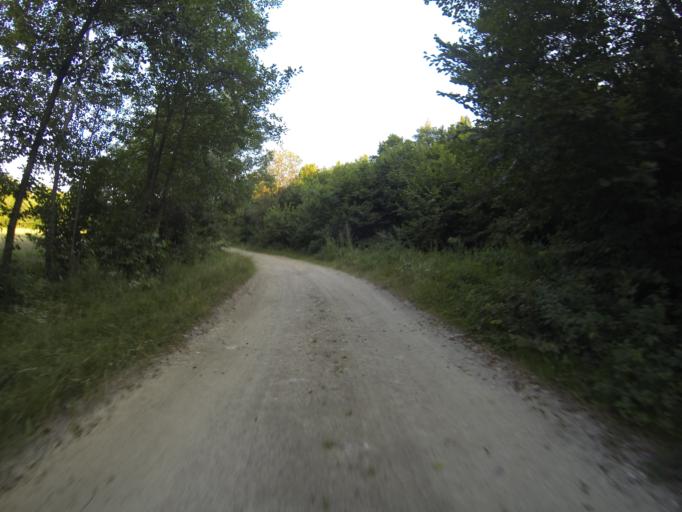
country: RO
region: Brasov
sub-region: Comuna Sinca Veche
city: Sinca Veche
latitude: 45.7405
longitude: 25.1956
